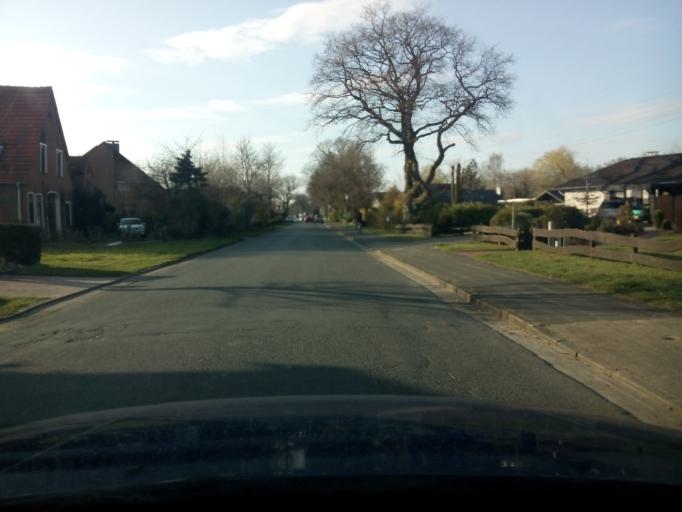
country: DE
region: Lower Saxony
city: Osterholz-Scharmbeck
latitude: 53.2284
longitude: 8.7586
